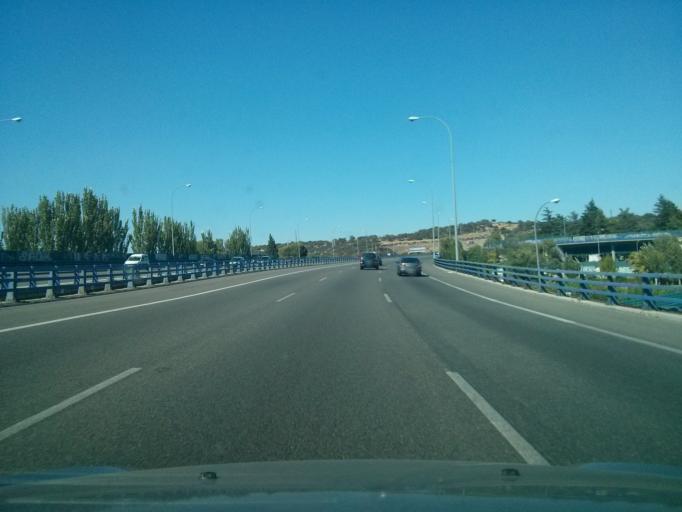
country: ES
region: Madrid
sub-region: Provincia de Madrid
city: Fuencarral-El Pardo
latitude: 40.4770
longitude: -3.7540
